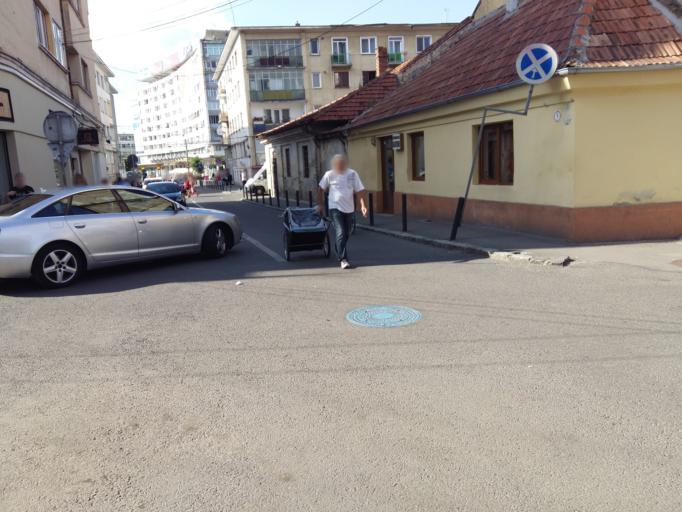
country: RO
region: Cluj
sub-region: Municipiul Cluj-Napoca
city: Cluj-Napoca
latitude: 46.7733
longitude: 23.5907
